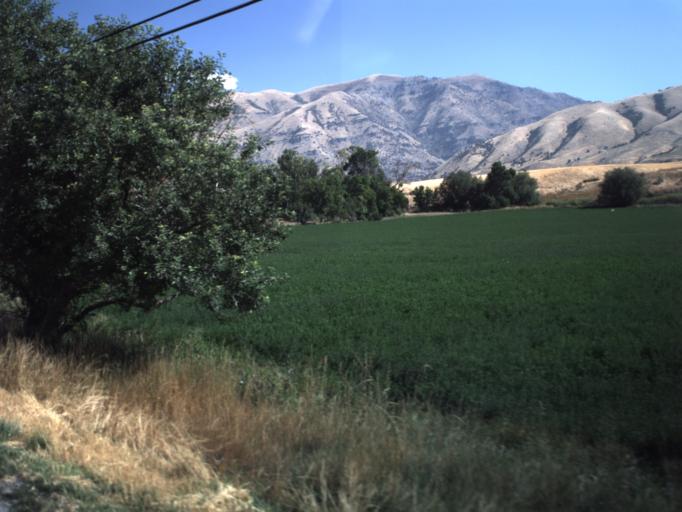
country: US
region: Utah
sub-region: Cache County
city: Hyrum
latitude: 41.6020
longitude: -111.8338
